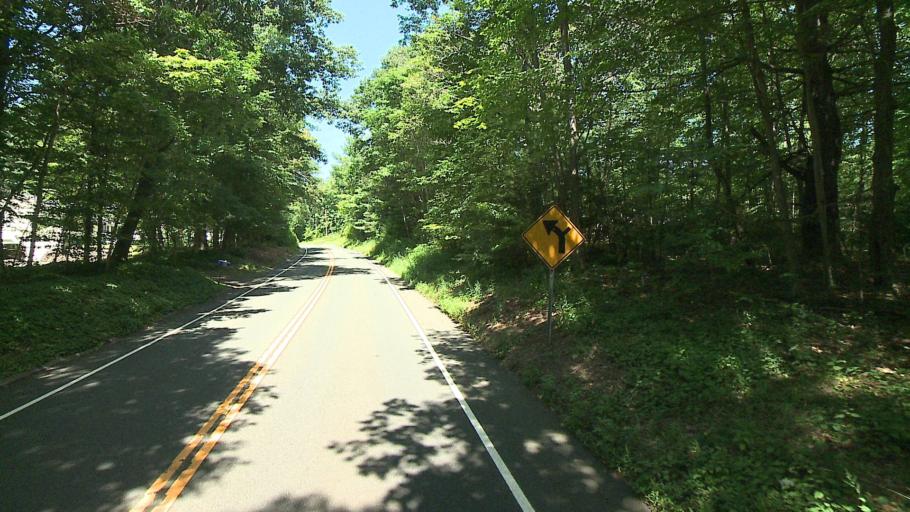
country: US
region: Connecticut
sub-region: Litchfield County
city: New Hartford Center
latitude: 41.9358
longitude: -72.9705
